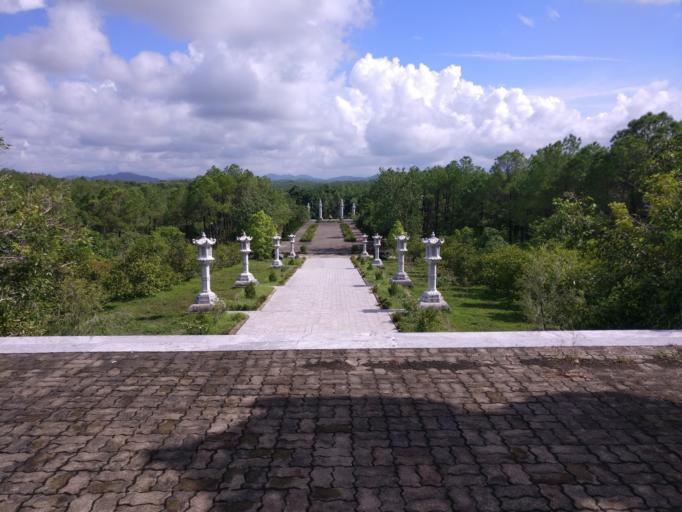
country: VN
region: Thua Thien-Hue
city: Hue
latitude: 16.4206
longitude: 107.6089
